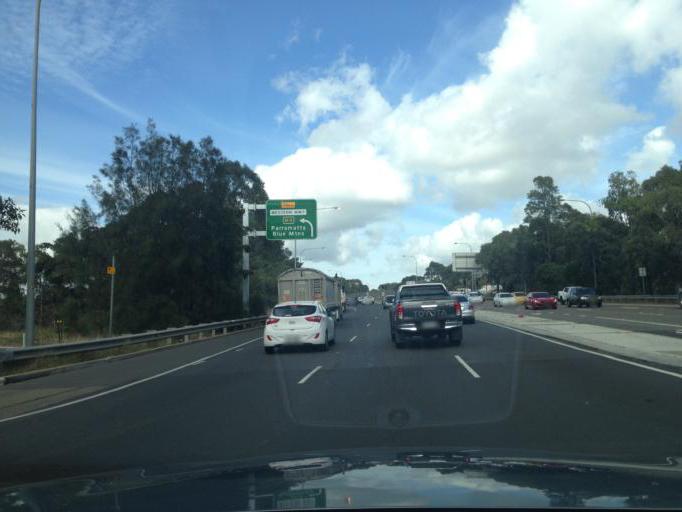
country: AU
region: New South Wales
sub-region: Strathfield
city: Homebush
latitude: -33.8560
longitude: 151.0725
